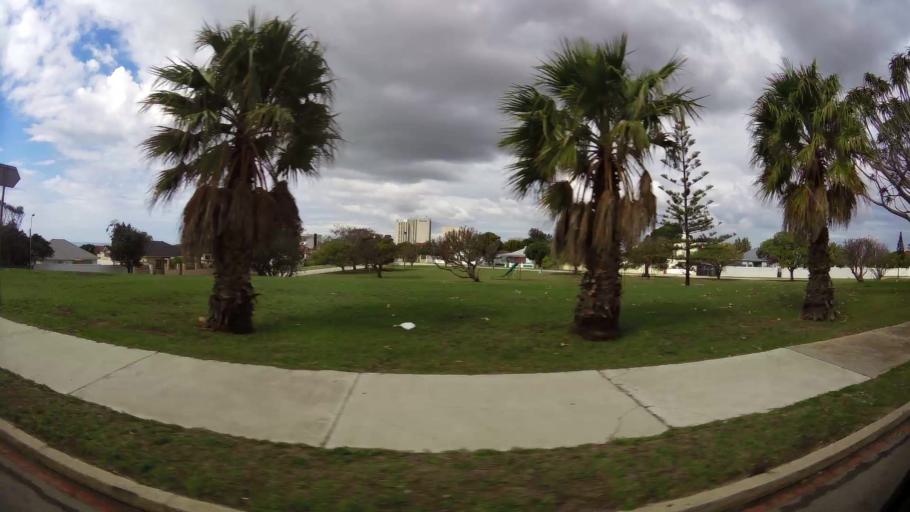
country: ZA
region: Eastern Cape
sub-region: Nelson Mandela Bay Metropolitan Municipality
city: Port Elizabeth
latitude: -33.9556
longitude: 25.5958
